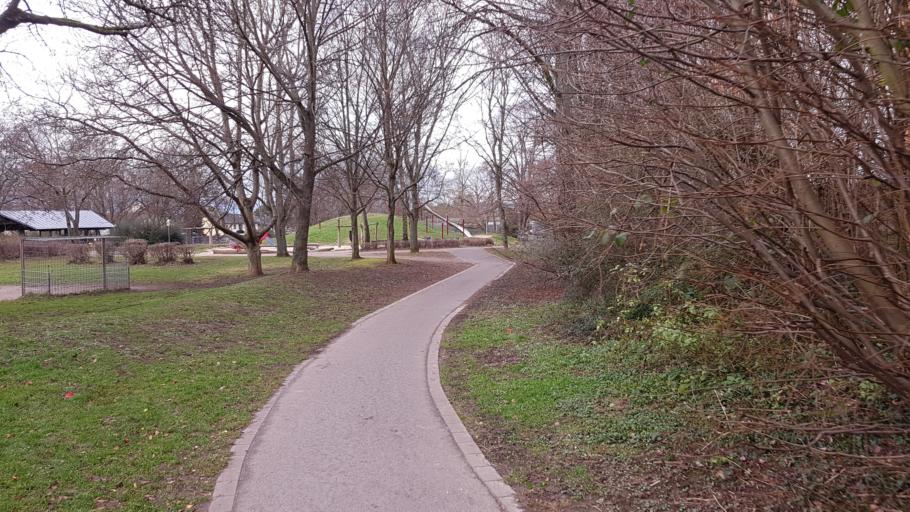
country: DE
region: Hesse
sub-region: Regierungsbezirk Darmstadt
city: Frankfurt am Main
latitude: 50.1477
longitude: 8.6869
